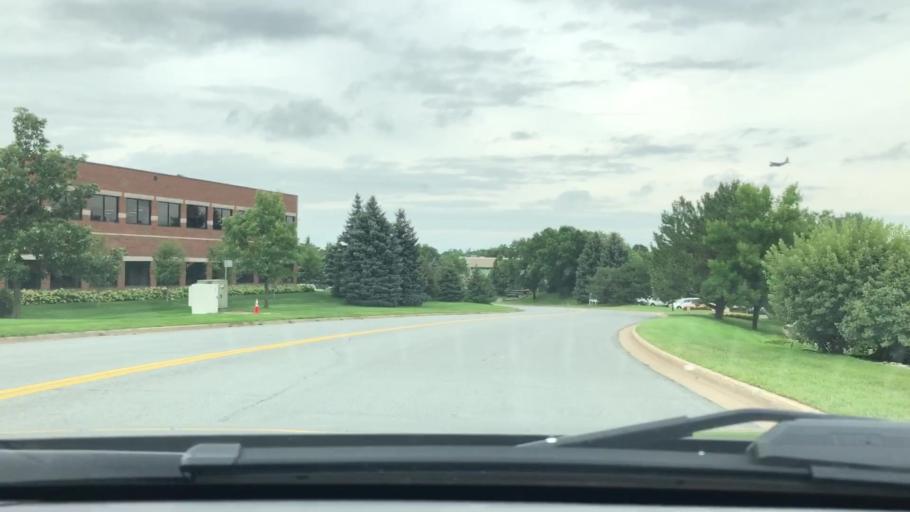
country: US
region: Minnesota
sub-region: Dakota County
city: Mendota Heights
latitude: 44.8555
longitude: -93.1604
